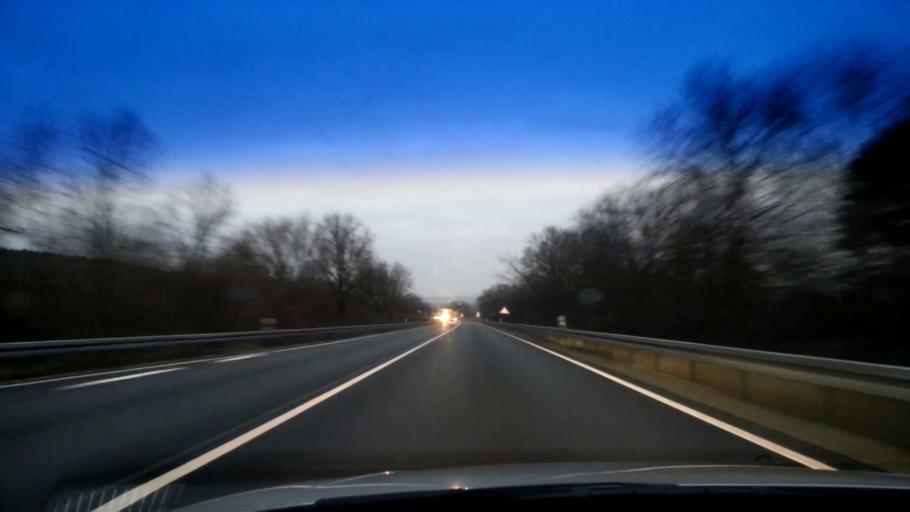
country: DE
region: Bavaria
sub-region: Upper Franconia
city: Hirschaid
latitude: 49.8060
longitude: 10.9594
